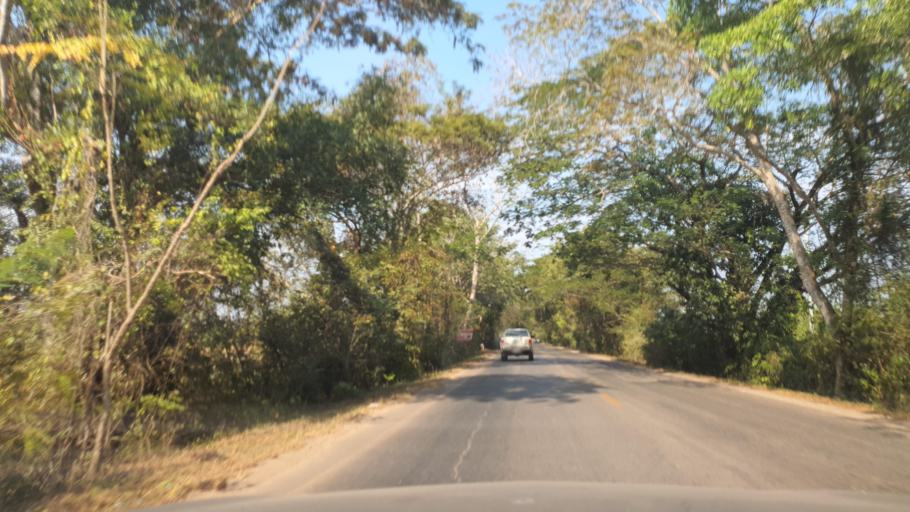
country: TH
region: Nakhon Phanom
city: Ban Phaeng
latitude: 18.0214
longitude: 104.1497
